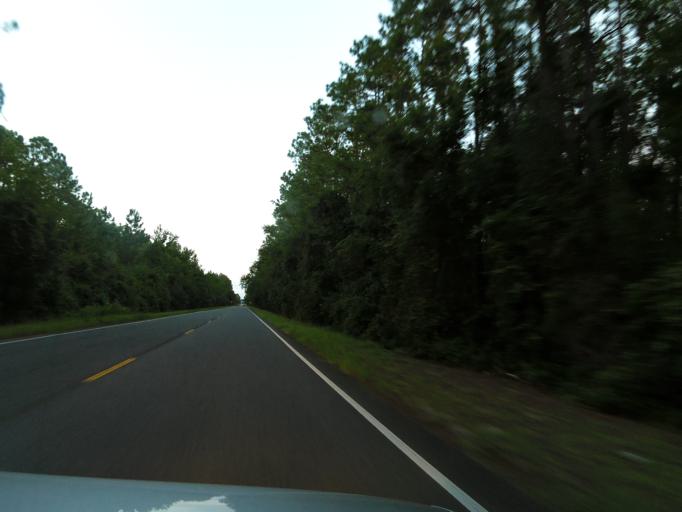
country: US
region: Georgia
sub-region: Camden County
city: Kingsland
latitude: 30.7530
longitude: -81.6876
